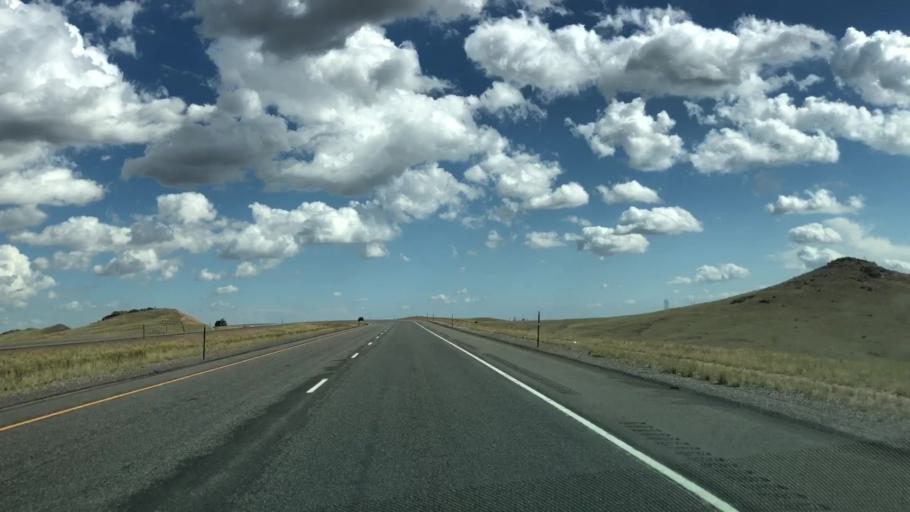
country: US
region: Wyoming
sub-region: Albany County
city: Laramie
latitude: 41.0463
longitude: -105.4634
